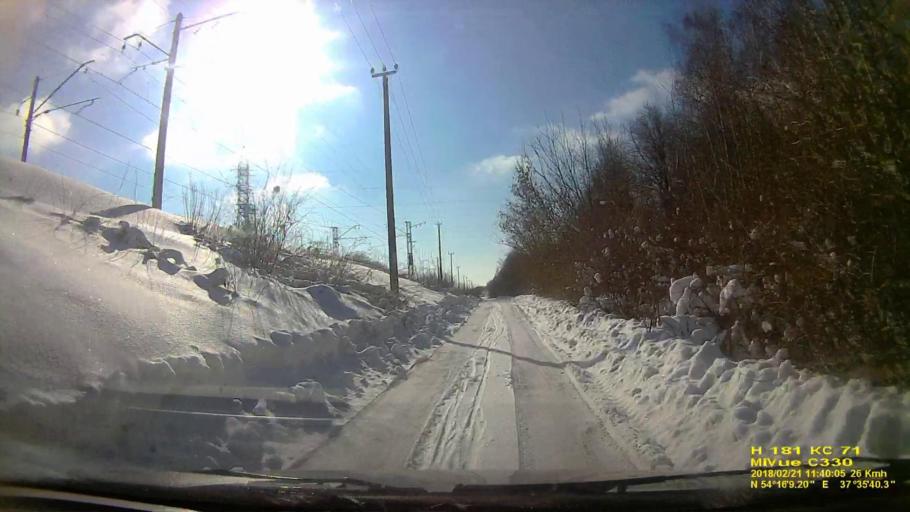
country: RU
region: Tula
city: Gorelki
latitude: 54.2691
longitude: 37.5945
